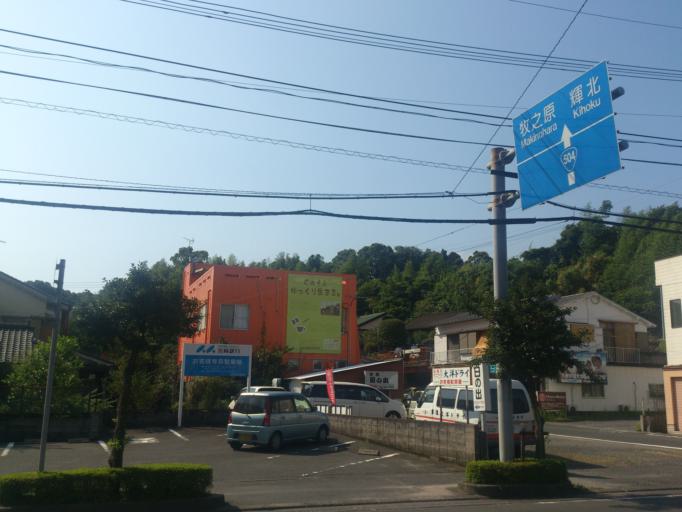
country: JP
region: Kagoshima
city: Kanoya
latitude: 31.3904
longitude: 130.8511
